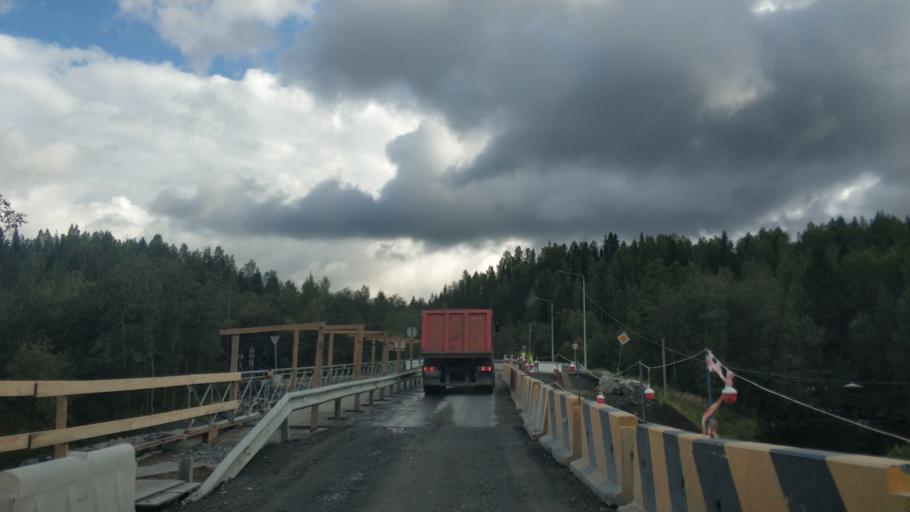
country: RU
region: Republic of Karelia
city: Ruskeala
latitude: 61.9374
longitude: 30.5902
